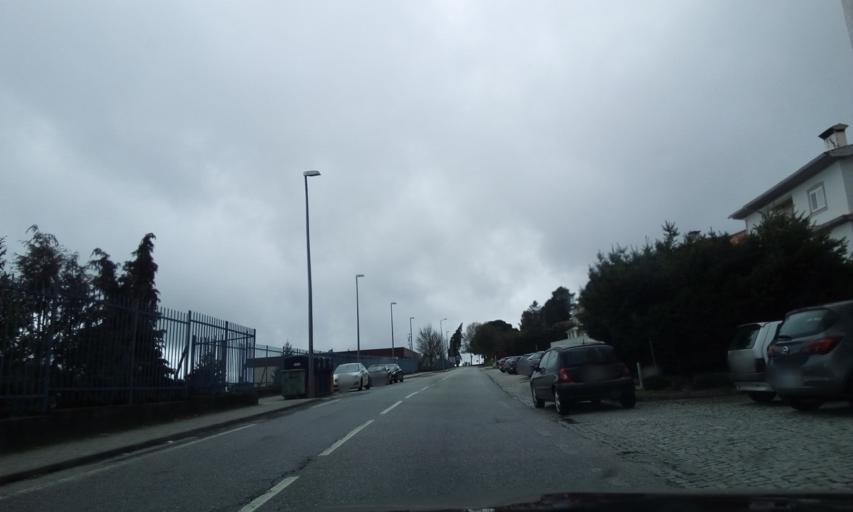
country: PT
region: Guarda
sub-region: Fornos de Algodres
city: Fornos de Algodres
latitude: 40.6160
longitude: -7.5448
